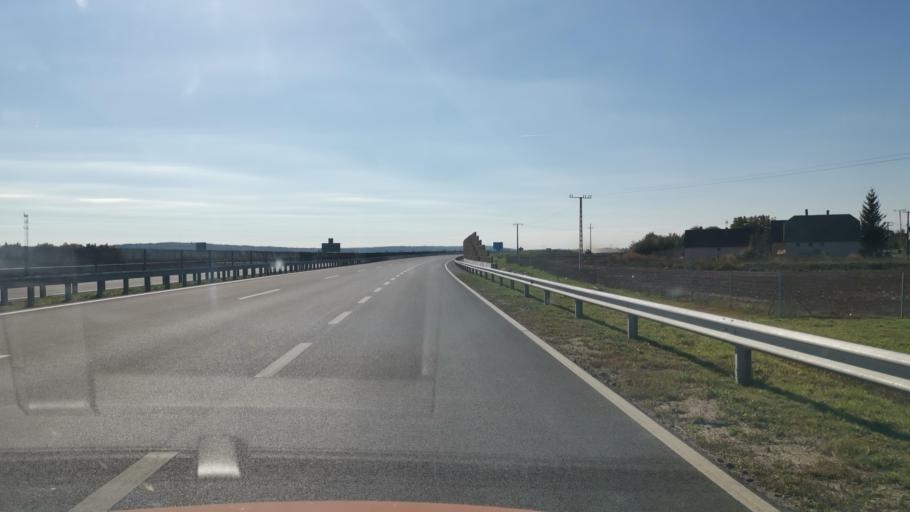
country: HU
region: Borsod-Abauj-Zemplen
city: Encs
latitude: 48.3292
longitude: 21.1019
